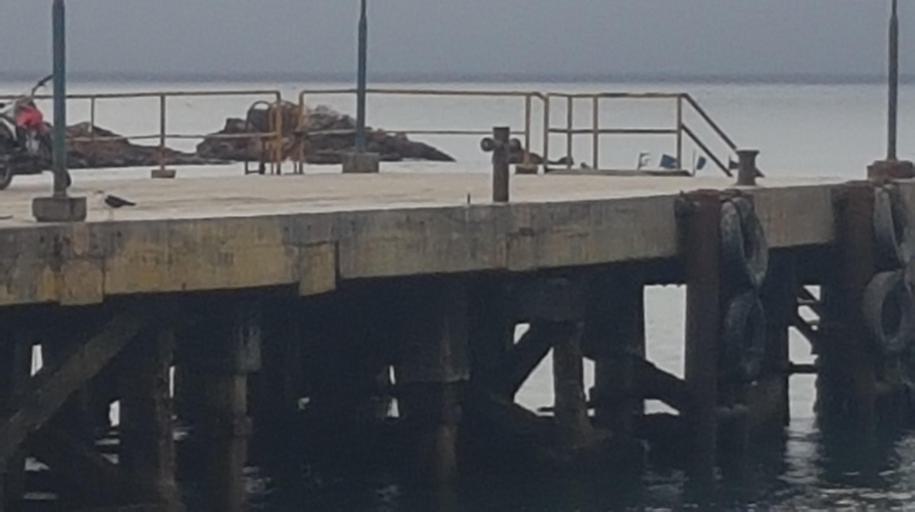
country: PE
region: Ancash
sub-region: Provincia de Huarmey
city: Huarmey
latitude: -10.0970
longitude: -78.1710
